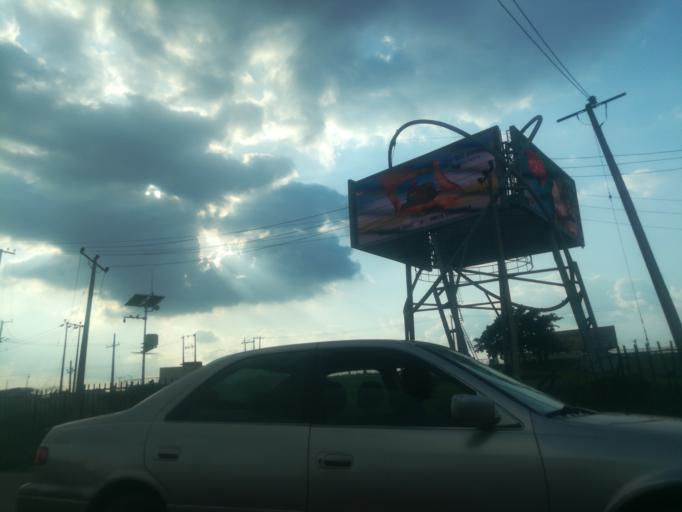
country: NG
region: Oyo
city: Ibadan
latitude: 7.4033
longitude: 3.9447
